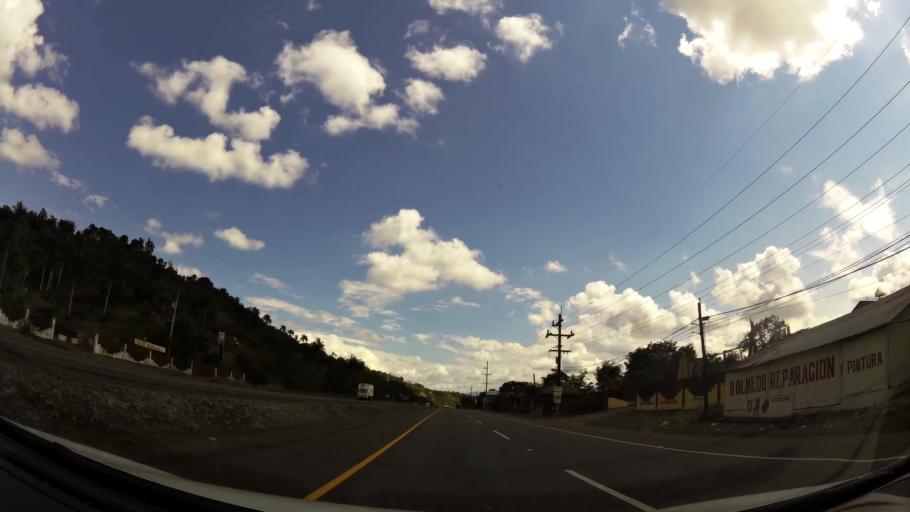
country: DO
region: La Vega
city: Rio Verde Arriba
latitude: 19.2849
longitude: -70.5731
